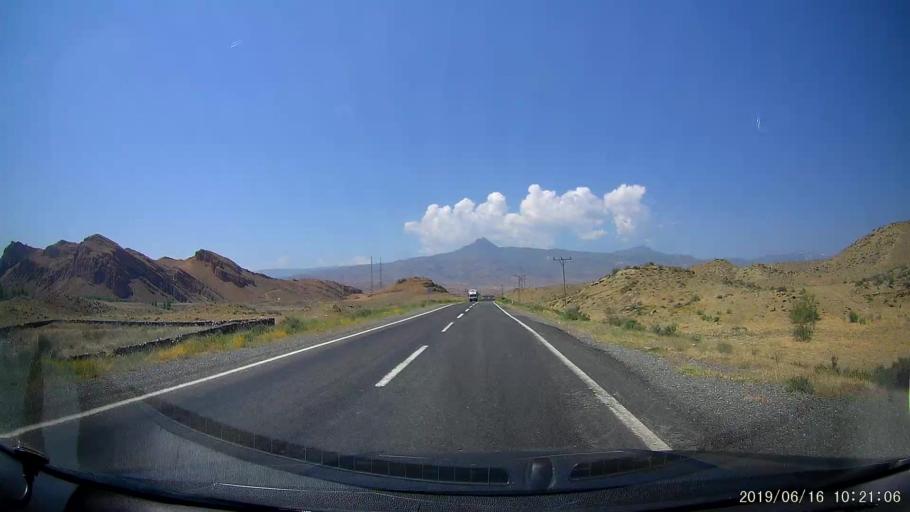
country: TR
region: Igdir
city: Tuzluca
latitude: 40.1409
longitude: 43.6403
